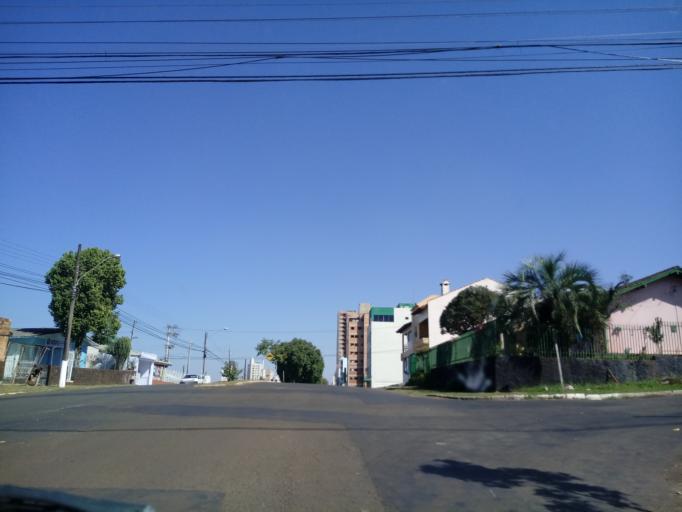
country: BR
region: Santa Catarina
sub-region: Chapeco
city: Chapeco
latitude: -27.0923
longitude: -52.6035
